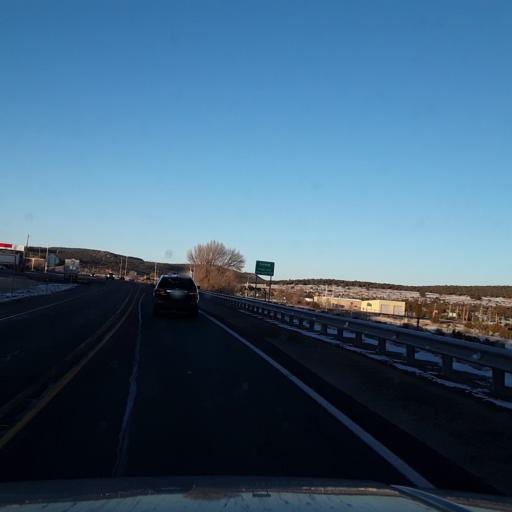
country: US
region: New Mexico
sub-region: Lincoln County
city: Carrizozo
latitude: 34.2428
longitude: -105.5959
